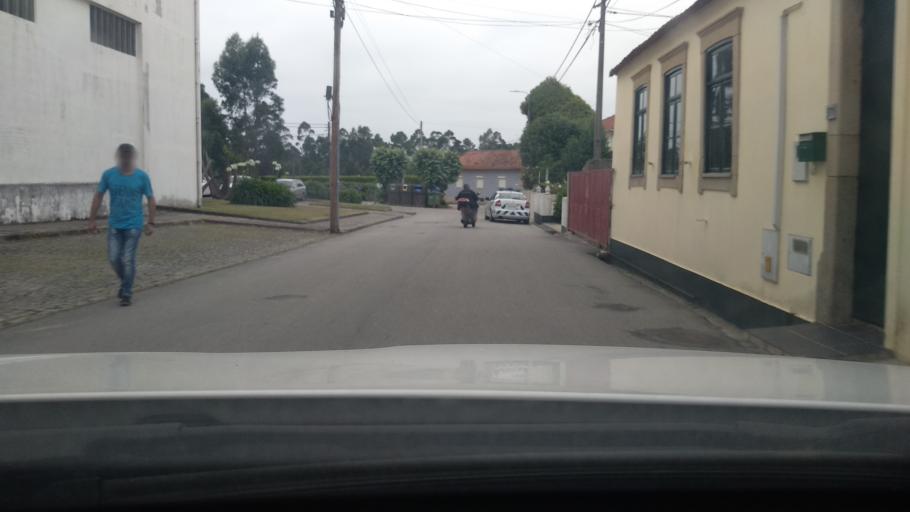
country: PT
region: Aveiro
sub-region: Espinho
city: Souto
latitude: 40.9850
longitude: -8.6223
